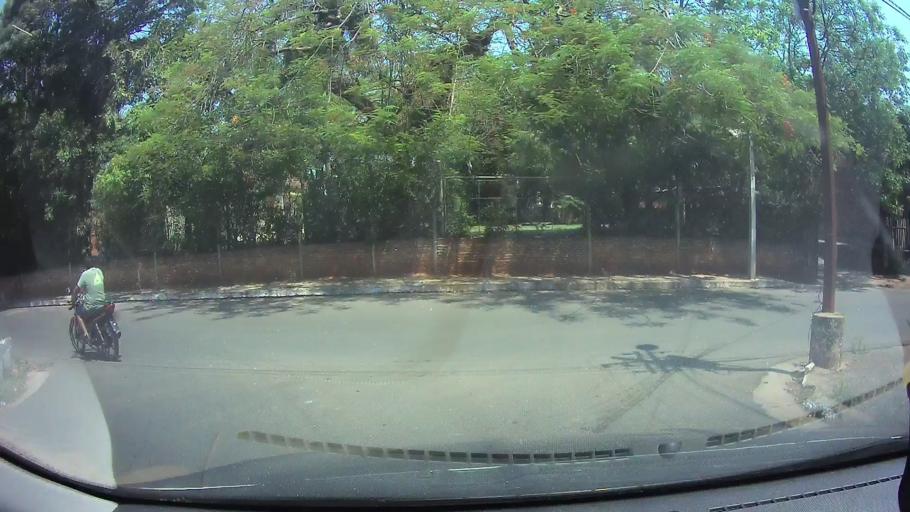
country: PY
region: Central
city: Fernando de la Mora
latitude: -25.3294
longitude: -57.5454
